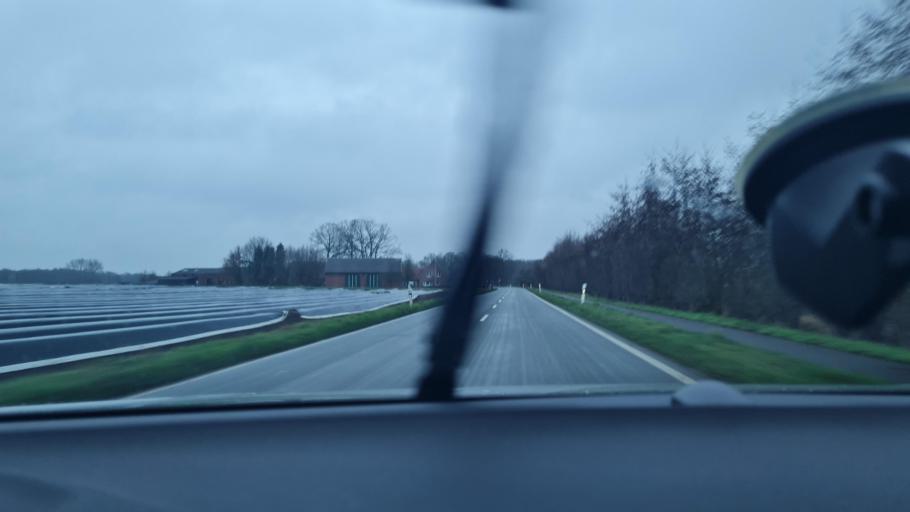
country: DE
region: North Rhine-Westphalia
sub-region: Regierungsbezirk Munster
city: Heiden
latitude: 51.7822
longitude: 6.9151
